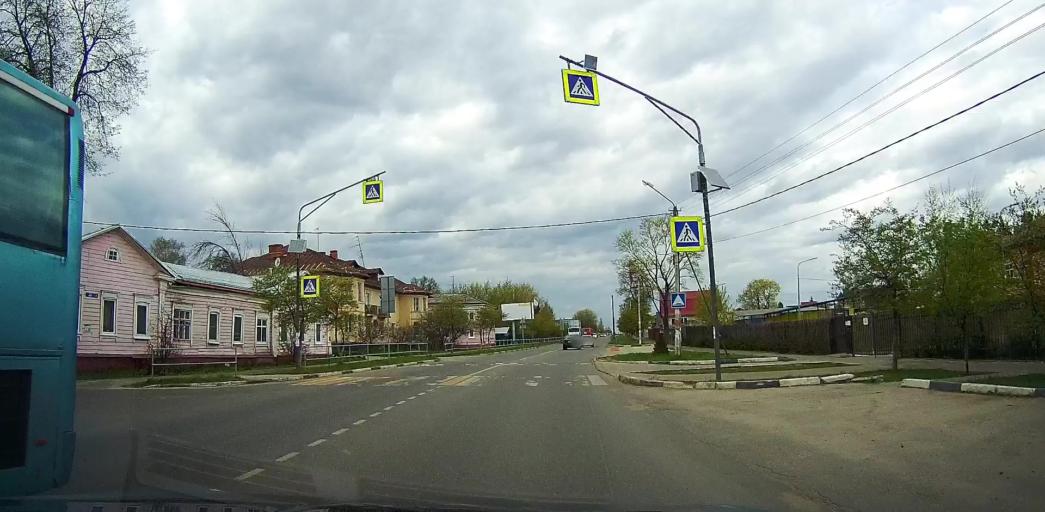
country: RU
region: Moskovskaya
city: Pavlovskiy Posad
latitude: 55.7855
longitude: 38.6482
